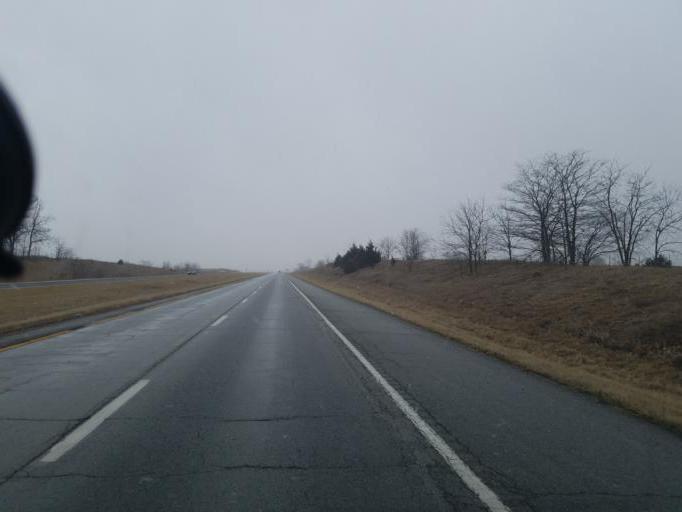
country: US
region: Missouri
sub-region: Macon County
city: La Plata
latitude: 39.9917
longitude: -92.4758
